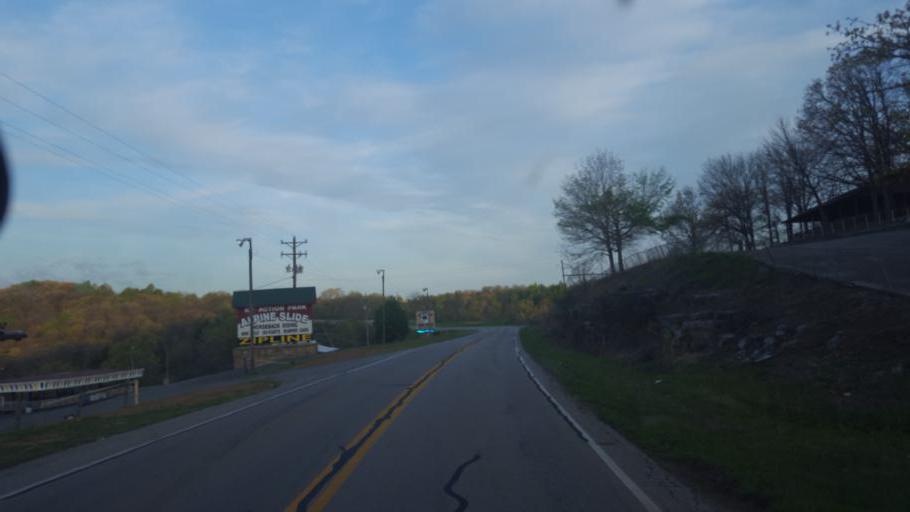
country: US
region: Kentucky
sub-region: Barren County
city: Cave City
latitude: 37.1333
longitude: -86.0041
